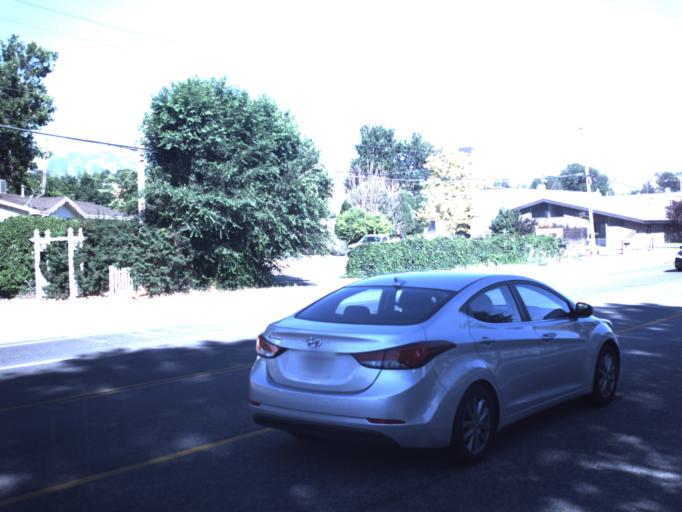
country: US
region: Utah
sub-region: Utah County
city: Lehi
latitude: 40.4082
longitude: -111.8631
